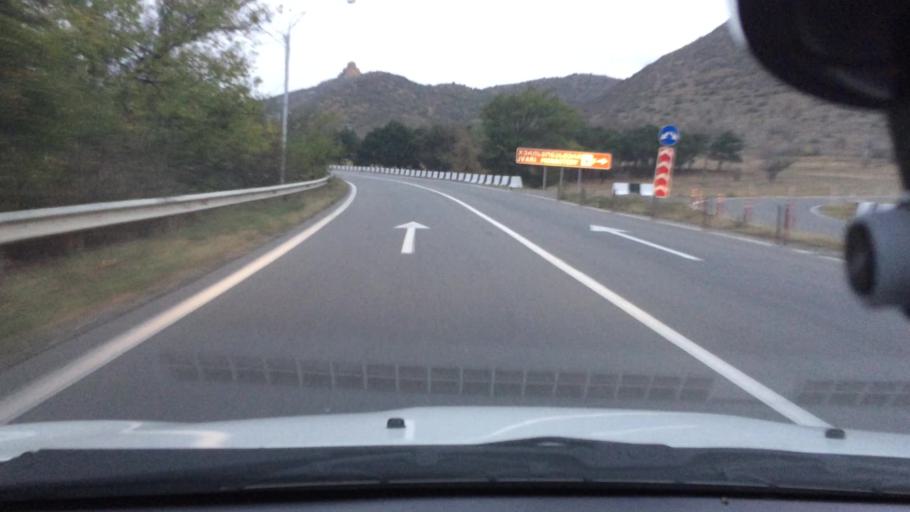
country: GE
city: Zahesi
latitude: 41.8276
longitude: 44.7359
